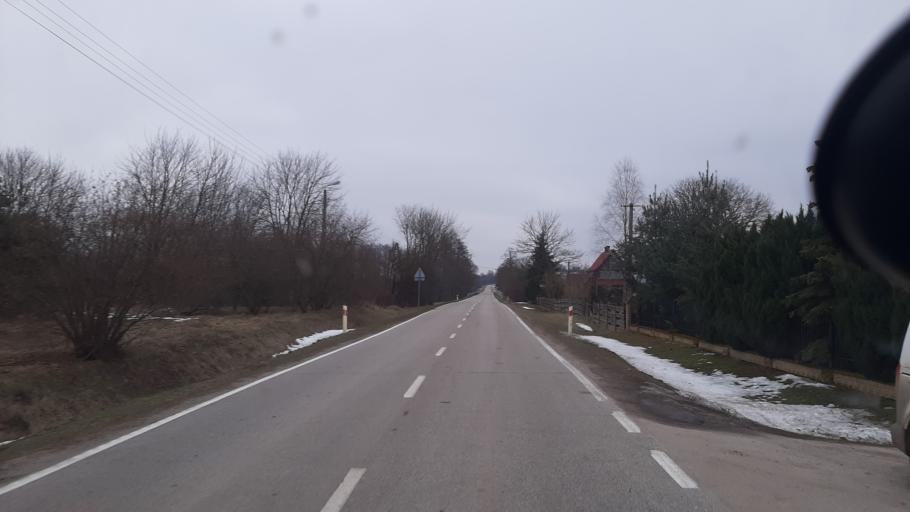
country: PL
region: Lublin Voivodeship
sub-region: Powiat wlodawski
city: Wlodawa
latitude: 51.4831
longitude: 23.6275
